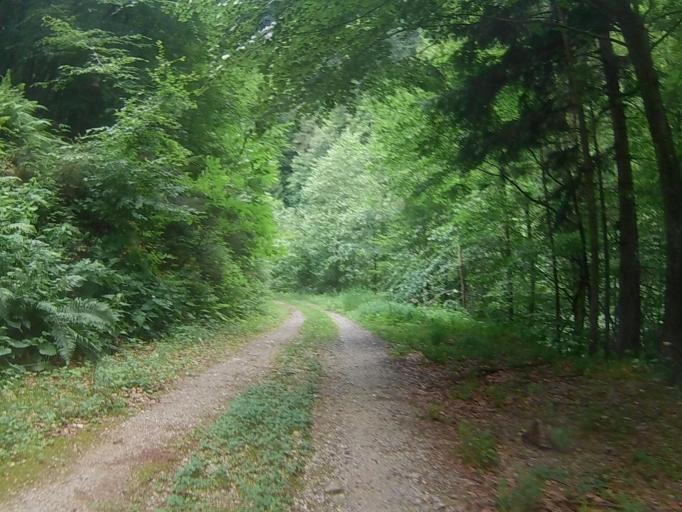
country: SI
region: Selnica ob Dravi
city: Selnica ob Dravi
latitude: 46.5184
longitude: 15.4858
